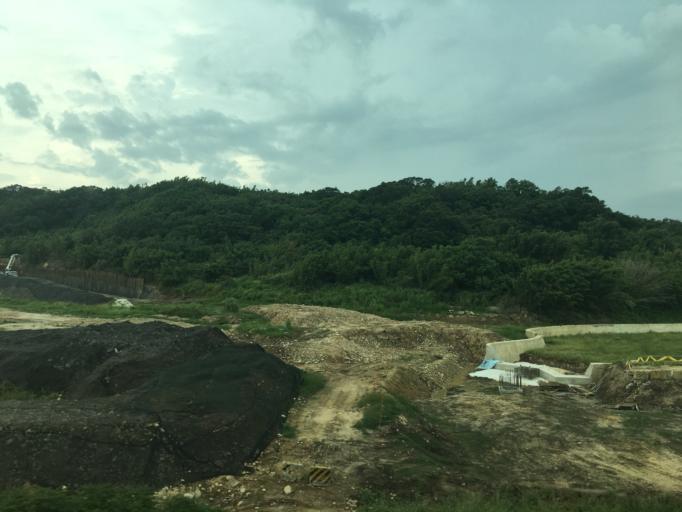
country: TW
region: Taiwan
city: Taoyuan City
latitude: 25.0807
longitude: 121.2876
